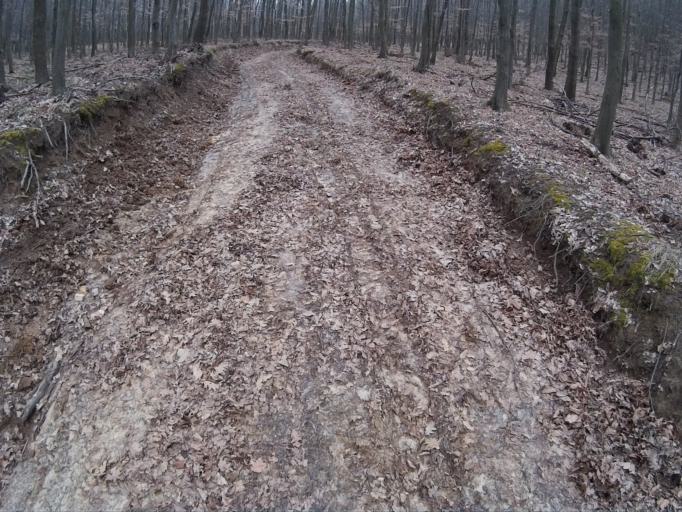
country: HU
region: Veszprem
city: Zirc
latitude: 47.1755
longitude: 17.8723
